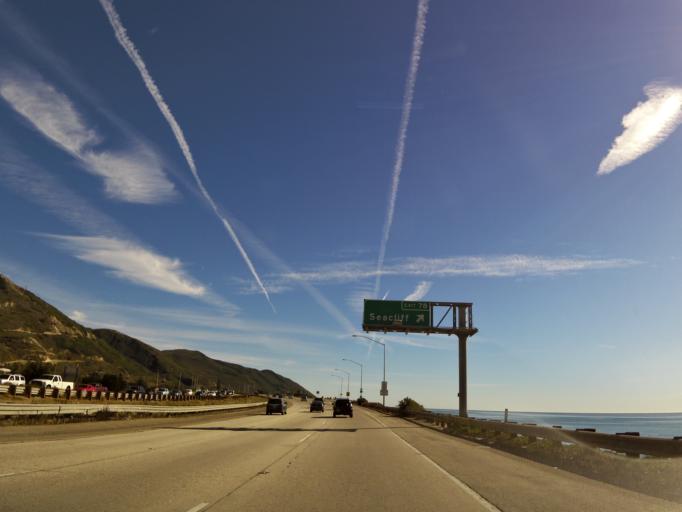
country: US
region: California
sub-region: Santa Barbara County
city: Carpinteria
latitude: 34.3455
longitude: -119.4214
